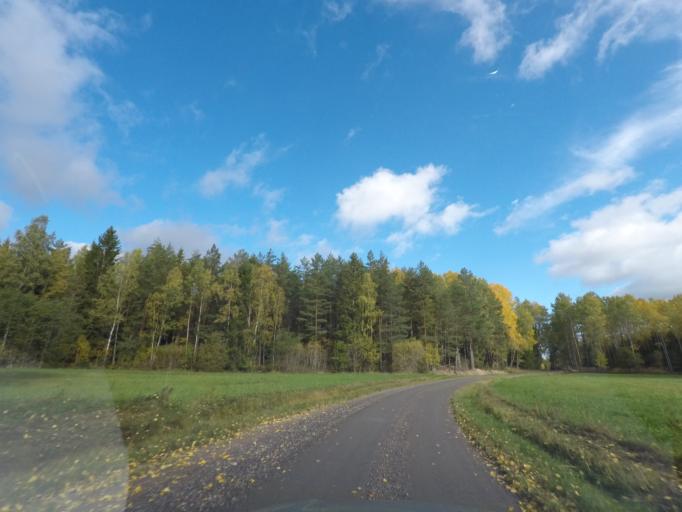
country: SE
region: Vaestmanland
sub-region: Kungsors Kommun
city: Kungsoer
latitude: 59.3373
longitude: 16.1612
